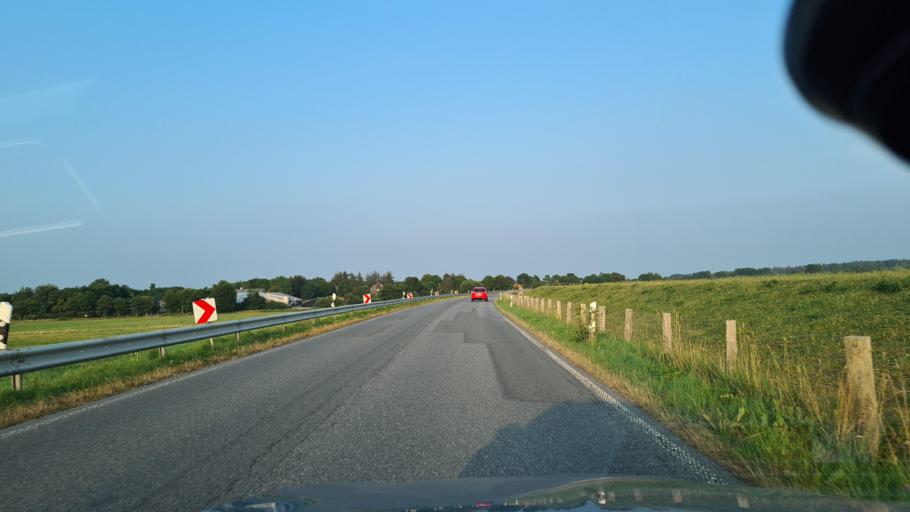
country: DE
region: Schleswig-Holstein
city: Wobbenbull
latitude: 54.5250
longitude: 8.9853
